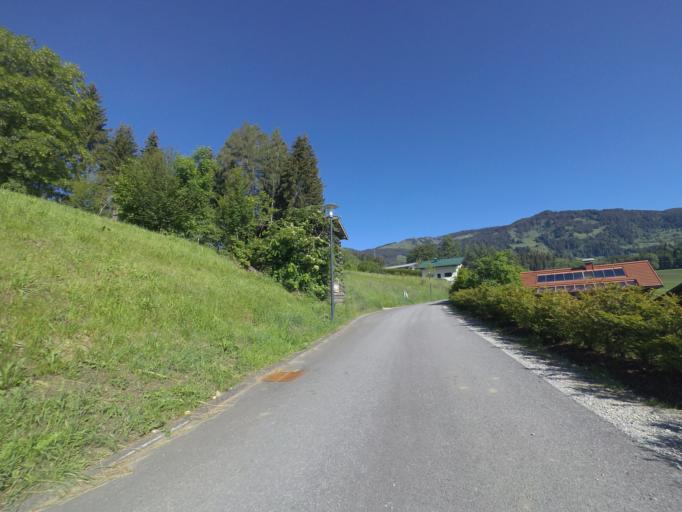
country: AT
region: Salzburg
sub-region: Politischer Bezirk Sankt Johann im Pongau
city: Goldegg
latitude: 47.3190
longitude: 13.0971
